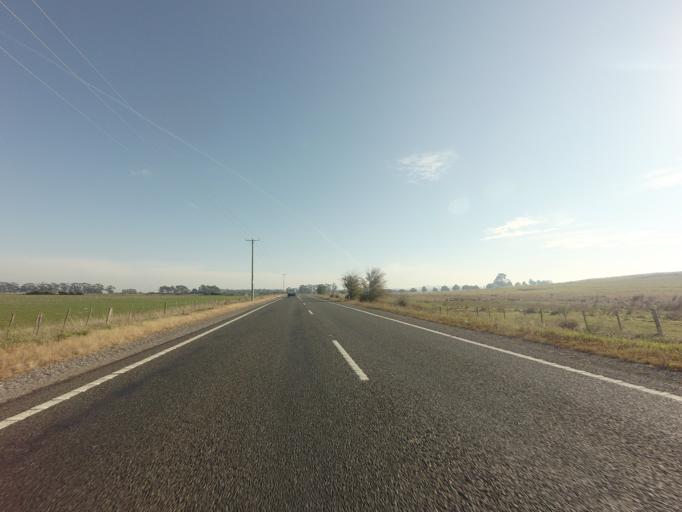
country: AU
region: Tasmania
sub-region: Northern Midlands
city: Longford
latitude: -41.5569
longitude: 147.0647
